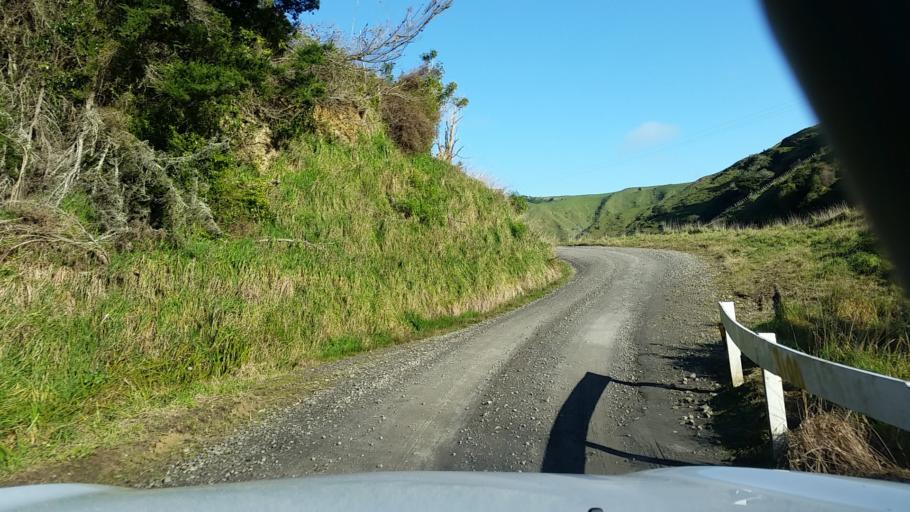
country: NZ
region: Taranaki
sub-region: South Taranaki District
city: Eltham
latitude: -39.5104
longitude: 174.3973
